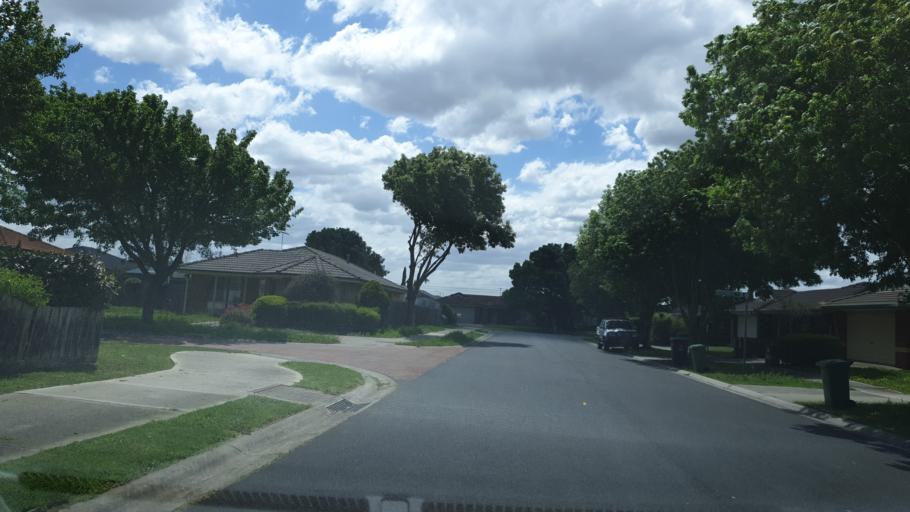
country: AU
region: Victoria
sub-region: Casey
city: Cranbourne
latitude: -38.0963
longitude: 145.2958
